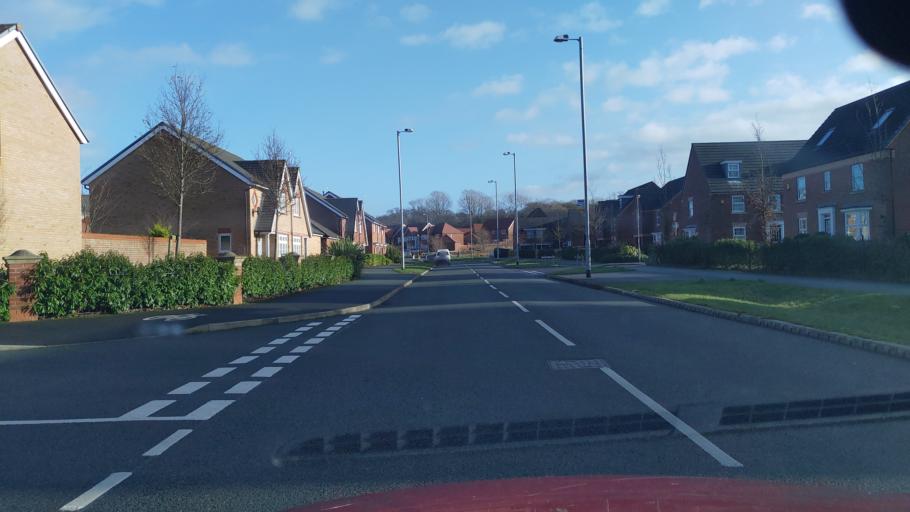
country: GB
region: England
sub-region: Lancashire
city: Clayton-le-Woods
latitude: 53.6798
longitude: -2.6548
